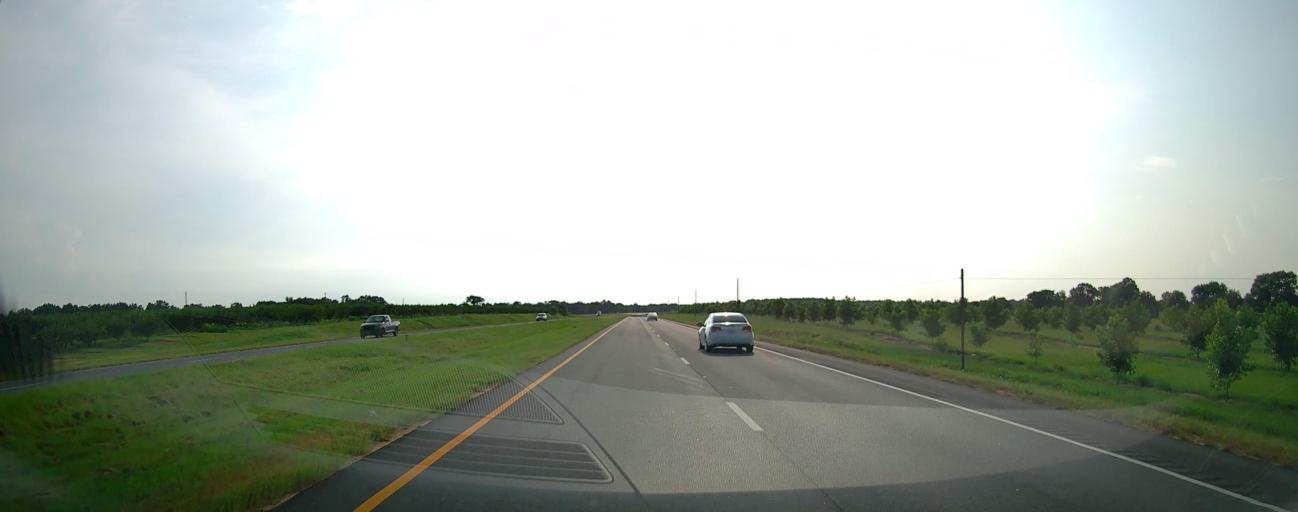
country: US
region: Georgia
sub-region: Taylor County
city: Reynolds
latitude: 32.5629
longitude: -84.1230
